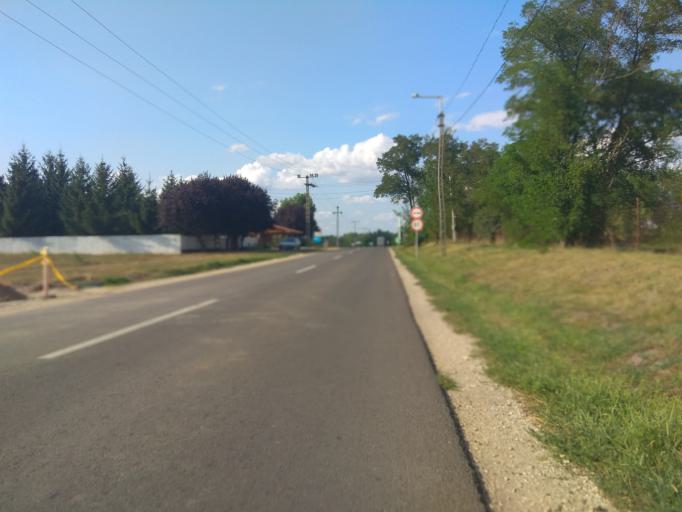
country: HU
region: Borsod-Abauj-Zemplen
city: Mezocsat
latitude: 47.8353
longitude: 20.9004
